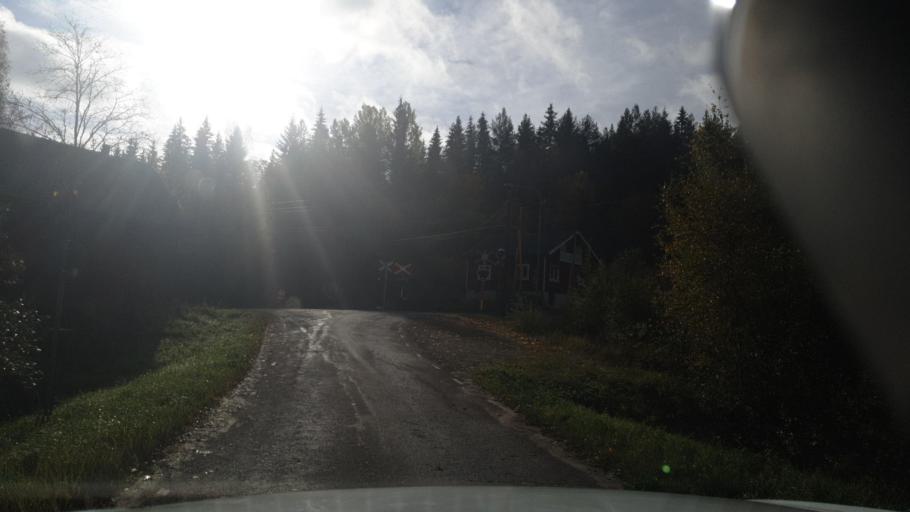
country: SE
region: Vaermland
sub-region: Sunne Kommun
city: Sunne
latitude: 59.6180
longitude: 12.9620
